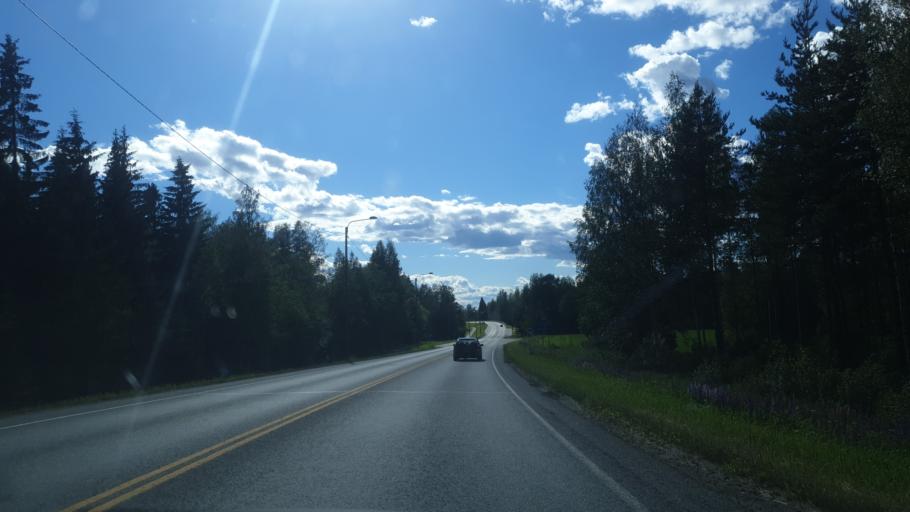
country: FI
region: Southern Savonia
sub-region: Mikkeli
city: Mikkeli
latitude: 61.7040
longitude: 27.3913
